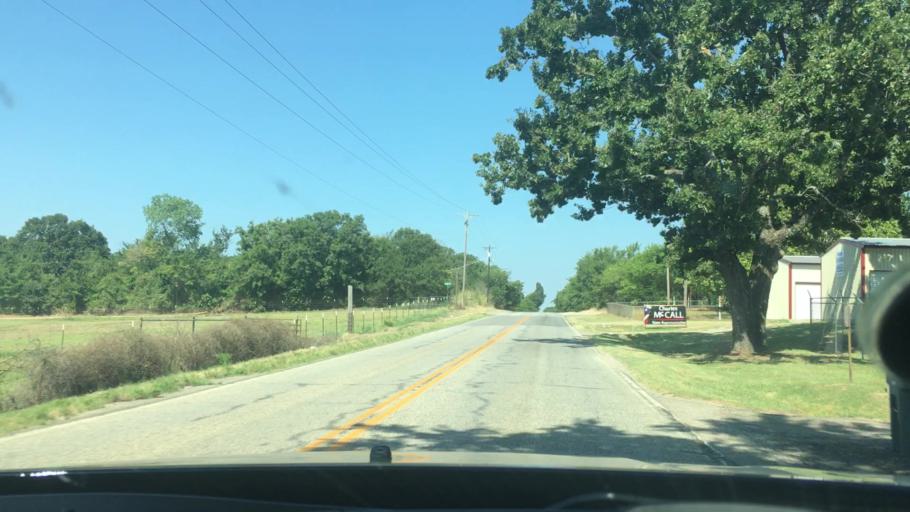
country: US
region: Oklahoma
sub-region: Johnston County
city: Tishomingo
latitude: 34.2377
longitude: -96.5649
